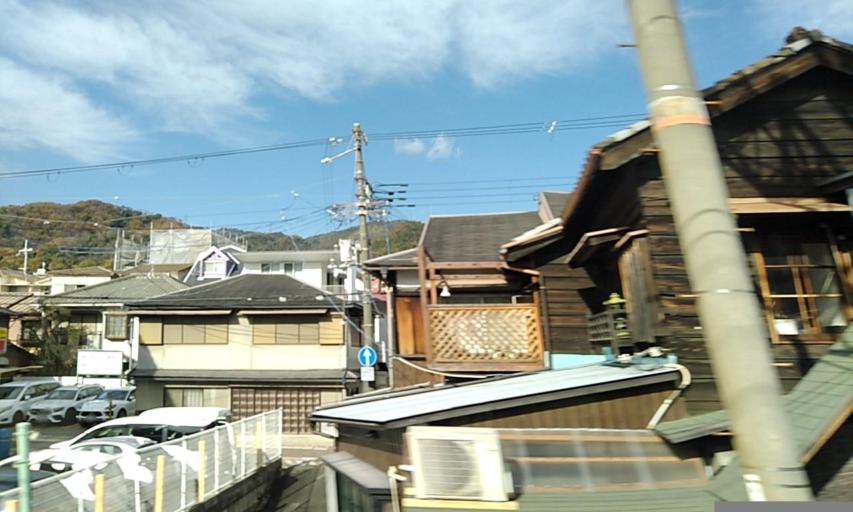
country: JP
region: Hyogo
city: Ashiya
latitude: 34.7360
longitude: 135.2997
